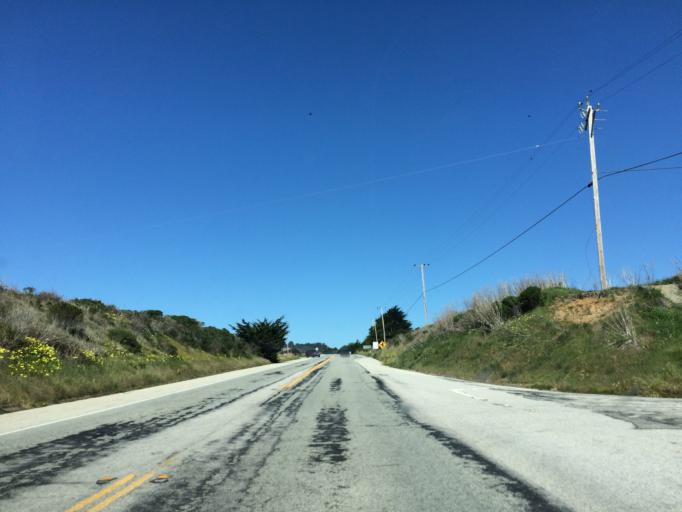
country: US
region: California
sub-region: Santa Cruz County
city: Boulder Creek
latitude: 37.1665
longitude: -122.3610
